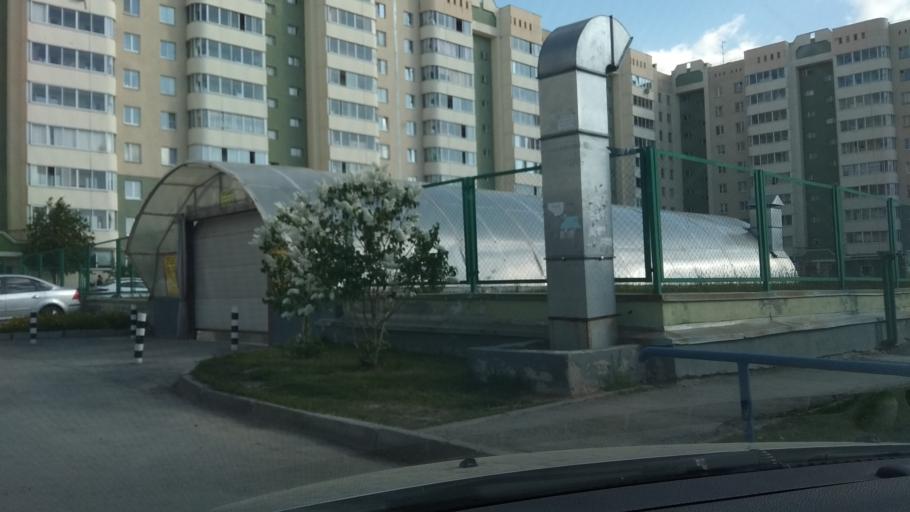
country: RU
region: Sverdlovsk
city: Sovkhoznyy
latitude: 56.7810
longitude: 60.5327
